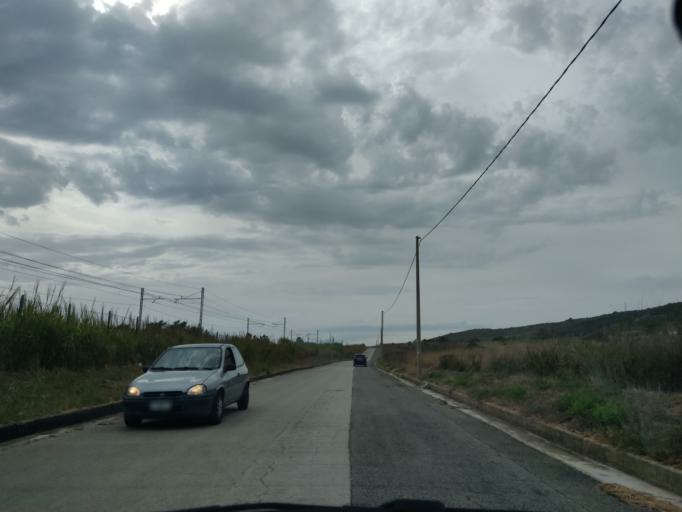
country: IT
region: Latium
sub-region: Citta metropolitana di Roma Capitale
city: Santa Marinella
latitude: 42.0398
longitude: 11.9178
